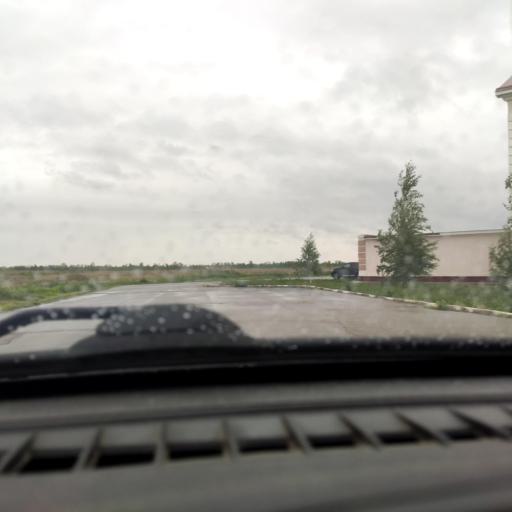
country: RU
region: Samara
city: Podstepki
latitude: 53.5291
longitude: 49.1770
